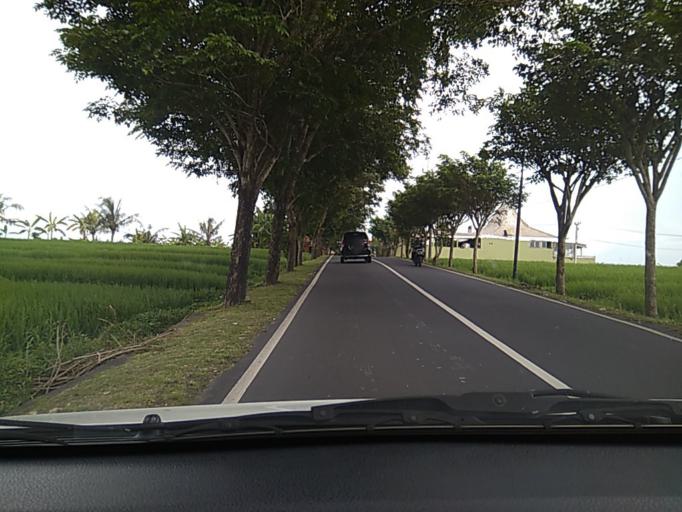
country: ID
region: Bali
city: Banjar Kerobokan
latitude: -8.6281
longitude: 115.1290
